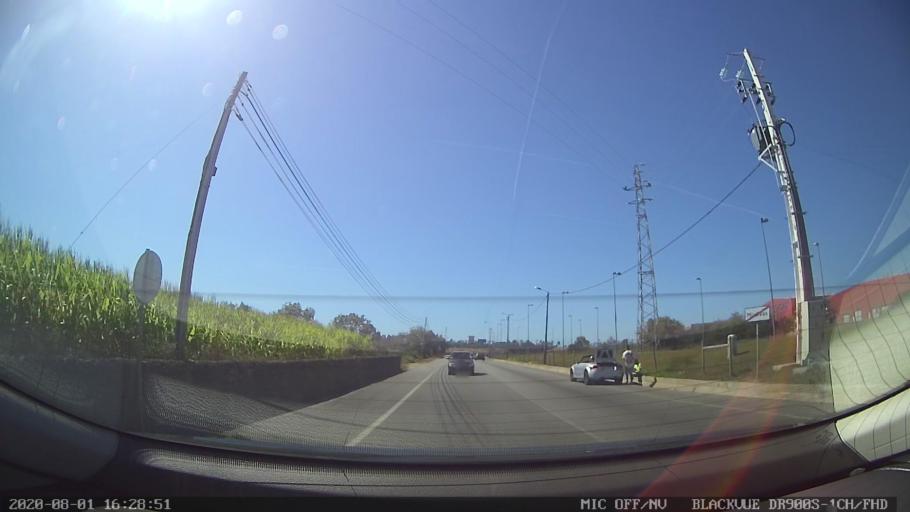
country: PT
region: Porto
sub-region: Matosinhos
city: Lavra
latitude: 41.2983
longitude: -8.6969
